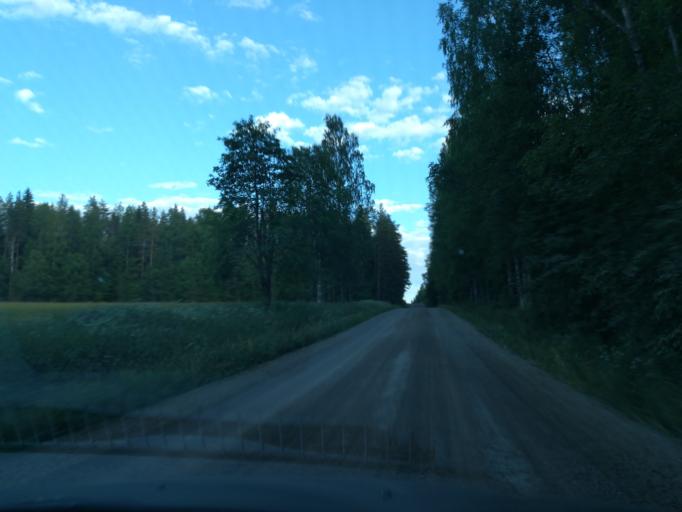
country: FI
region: Southern Savonia
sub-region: Mikkeli
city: Puumala
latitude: 61.5872
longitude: 28.1178
